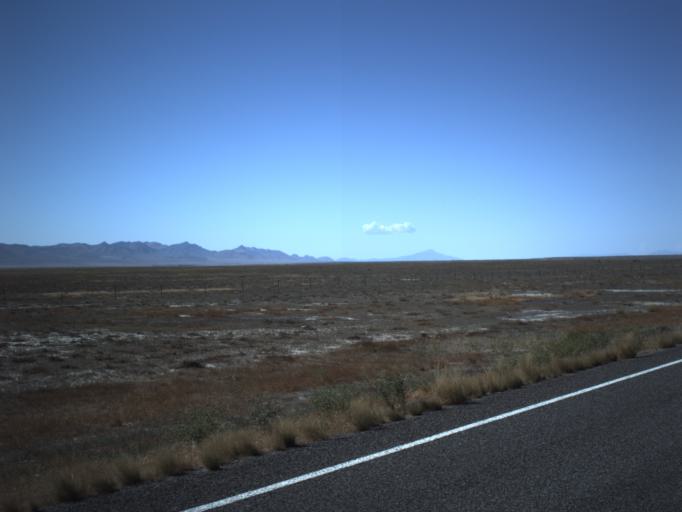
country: US
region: Utah
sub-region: Millard County
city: Delta
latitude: 39.2274
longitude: -112.9370
